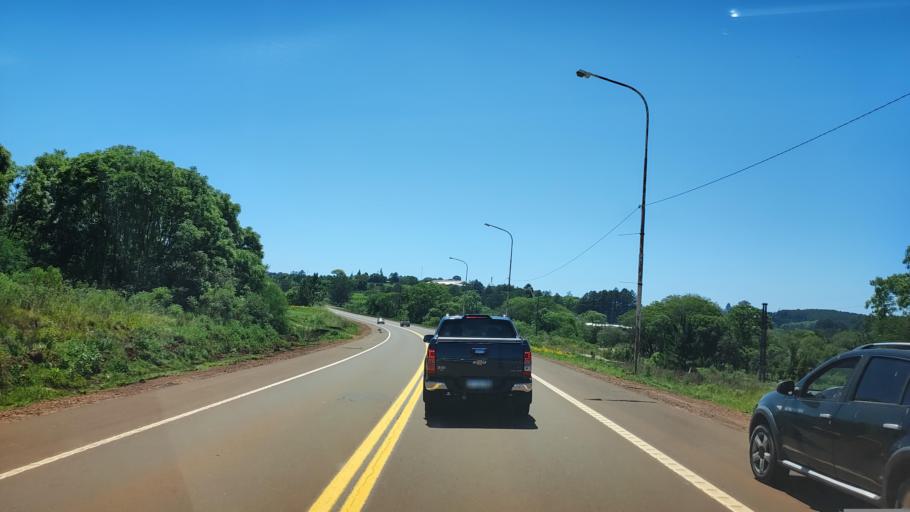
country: AR
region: Misiones
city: Aristobulo del Valle
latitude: -27.0873
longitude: -54.7873
